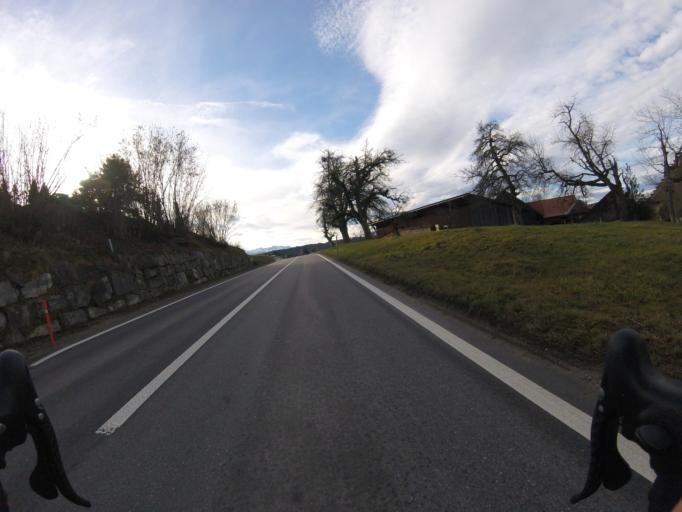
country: CH
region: Fribourg
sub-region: Sense District
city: Ueberstorf
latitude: 46.8574
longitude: 7.3162
